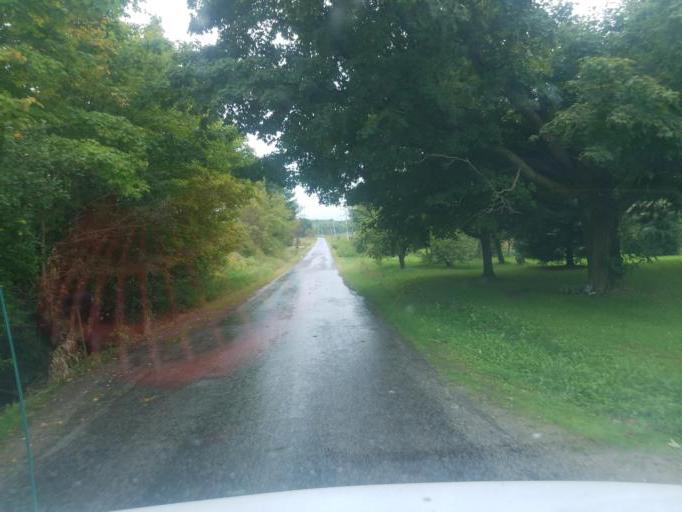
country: US
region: Ohio
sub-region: Wayne County
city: West Salem
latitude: 40.9293
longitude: -82.1521
